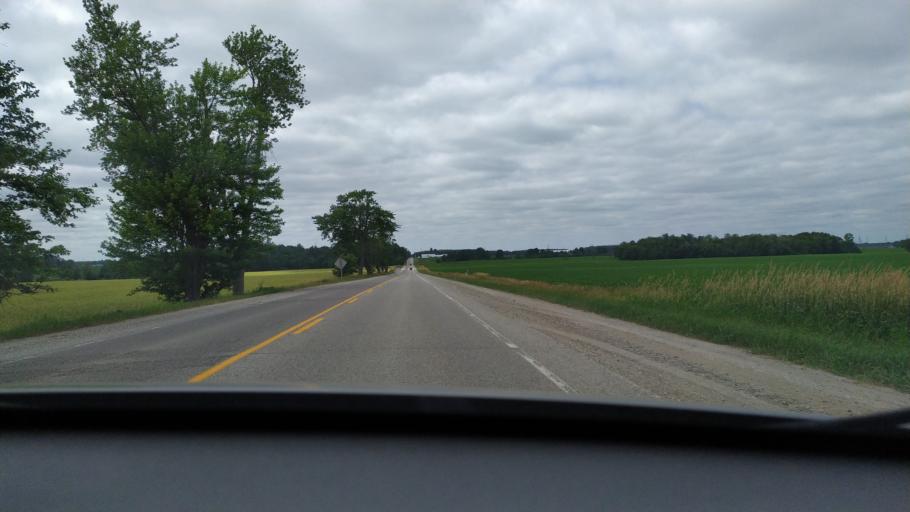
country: CA
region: Ontario
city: Stratford
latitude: 43.3177
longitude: -80.9524
